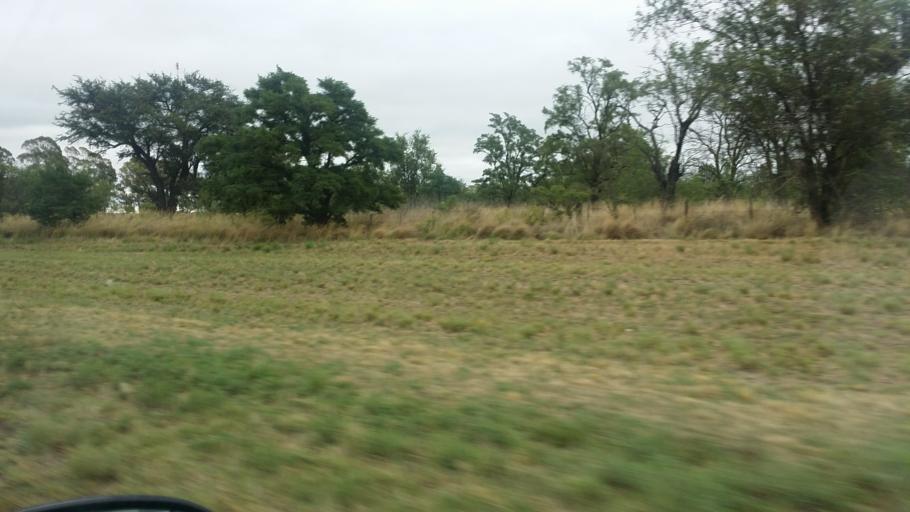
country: AR
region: La Pampa
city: Uriburu
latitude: -36.5139
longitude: -63.7389
